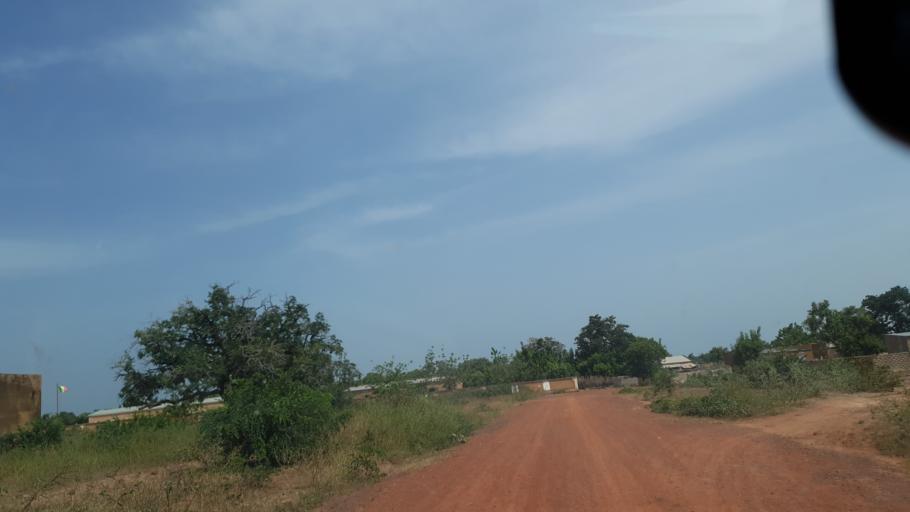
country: ML
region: Koulikoro
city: Dioila
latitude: 12.4771
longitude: -6.1846
